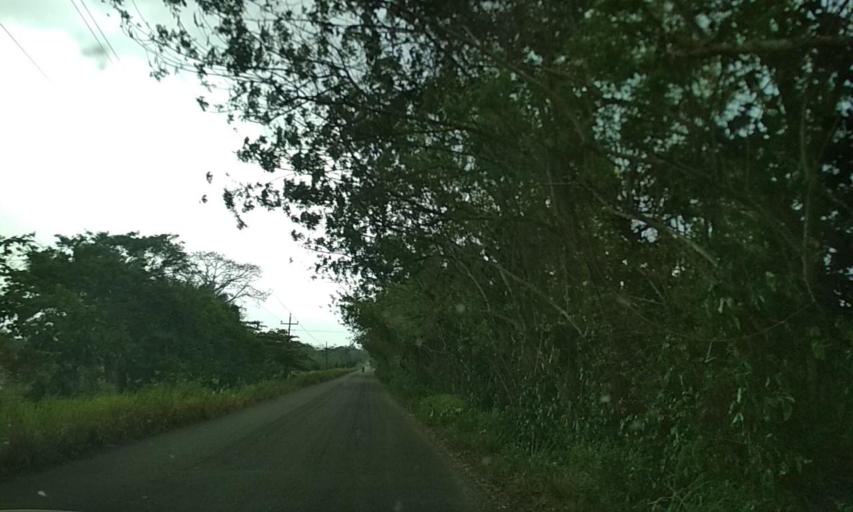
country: MX
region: Tabasco
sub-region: Huimanguillo
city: Francisco Rueda
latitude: 17.5600
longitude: -94.1180
